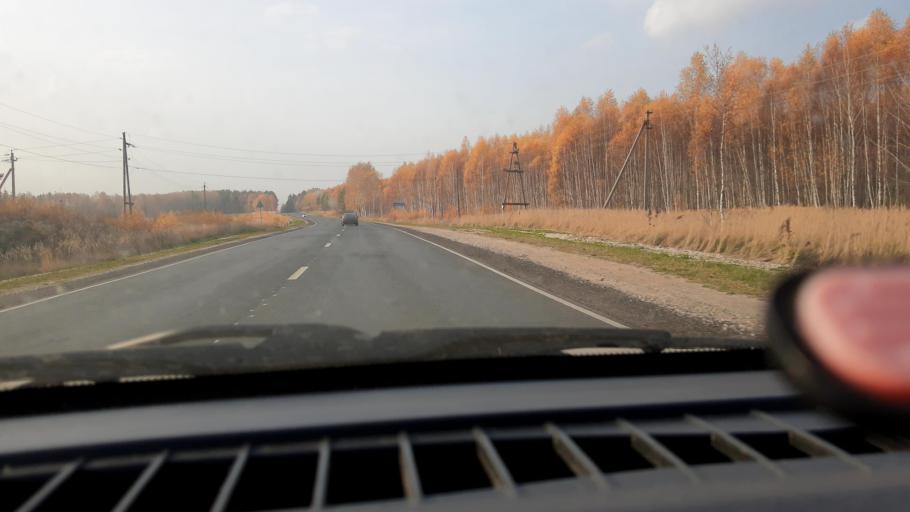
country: RU
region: Nizjnij Novgorod
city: Novaya Balakhna
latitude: 56.6114
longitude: 43.6010
